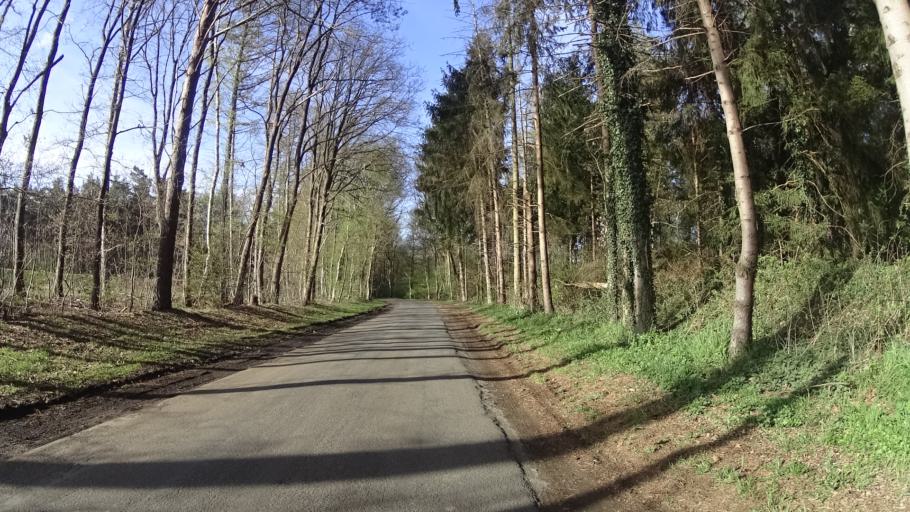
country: DE
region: Lower Saxony
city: Haren
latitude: 52.7685
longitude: 7.2684
